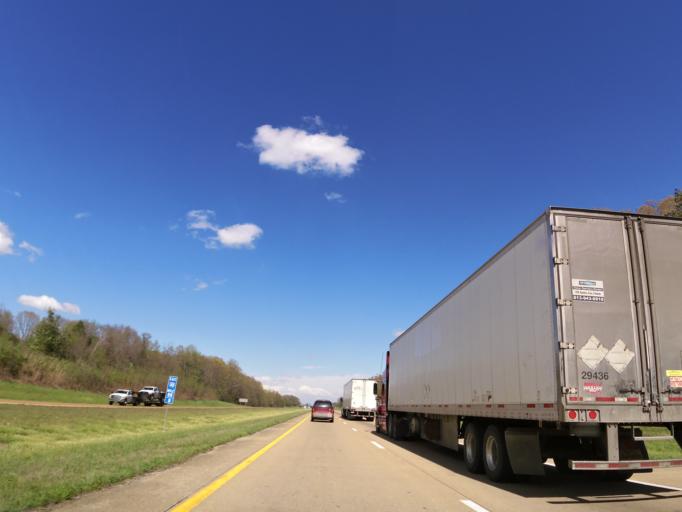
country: US
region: Tennessee
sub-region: Madison County
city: Jackson
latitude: 35.6910
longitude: -88.7102
